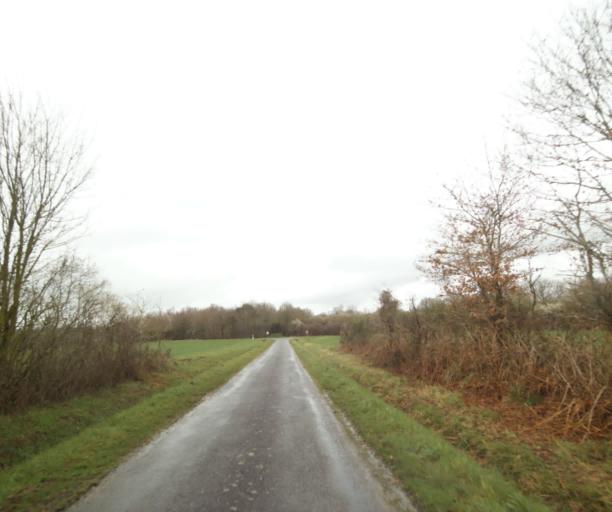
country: FR
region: Pays de la Loire
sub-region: Departement de la Loire-Atlantique
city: Bouvron
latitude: 47.4592
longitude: -1.8779
